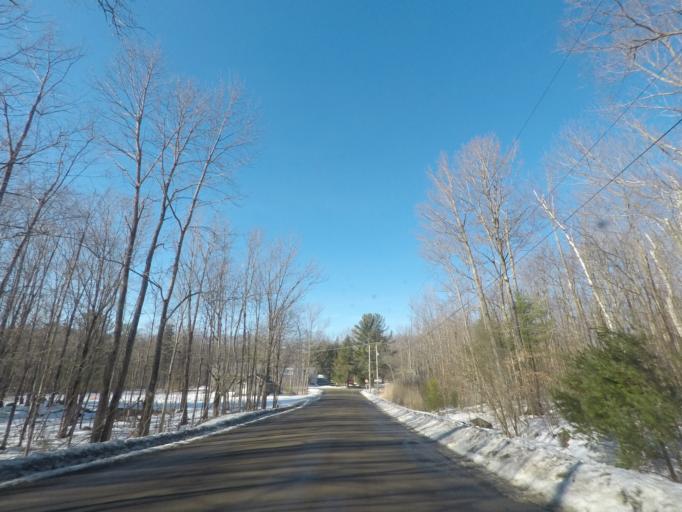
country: US
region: New York
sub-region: Rensselaer County
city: Averill Park
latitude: 42.6498
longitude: -73.5027
